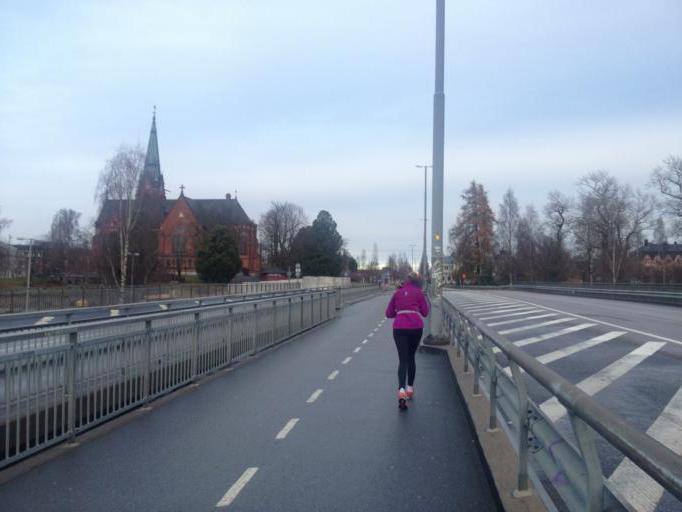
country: SE
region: Vaesterbotten
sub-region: Umea Kommun
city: Umea
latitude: 63.8220
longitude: 20.2680
